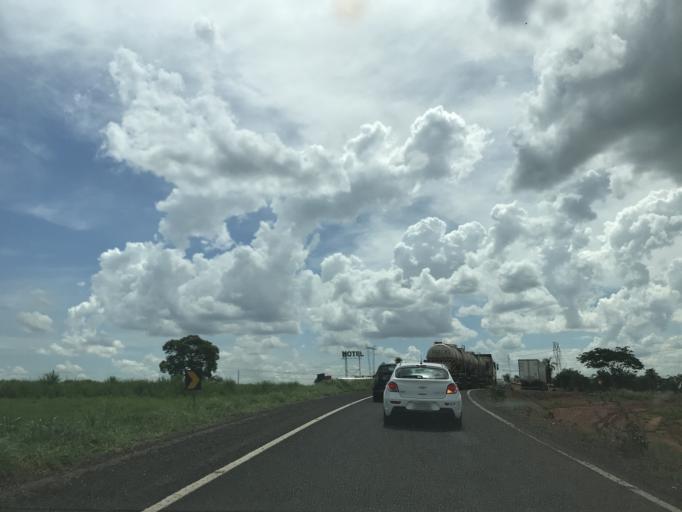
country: BR
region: Sao Paulo
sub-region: Nova Granada
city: Nova Granada
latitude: -20.3238
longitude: -49.2125
